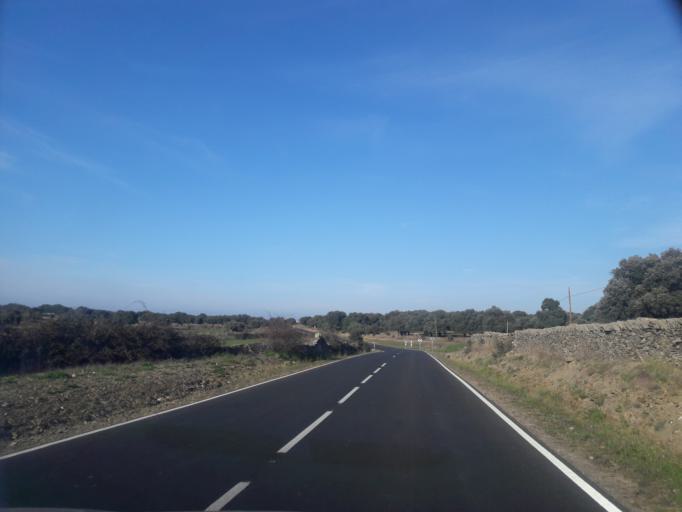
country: ES
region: Castille and Leon
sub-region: Provincia de Salamanca
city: Aldeavieja de Tormes
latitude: 40.5791
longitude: -5.6290
